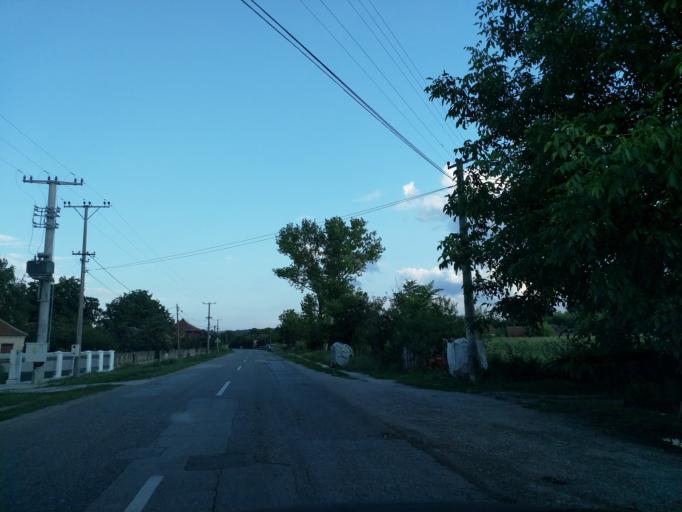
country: RS
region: Central Serbia
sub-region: Rasinski Okrug
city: Cicevac
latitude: 43.7563
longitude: 21.4348
